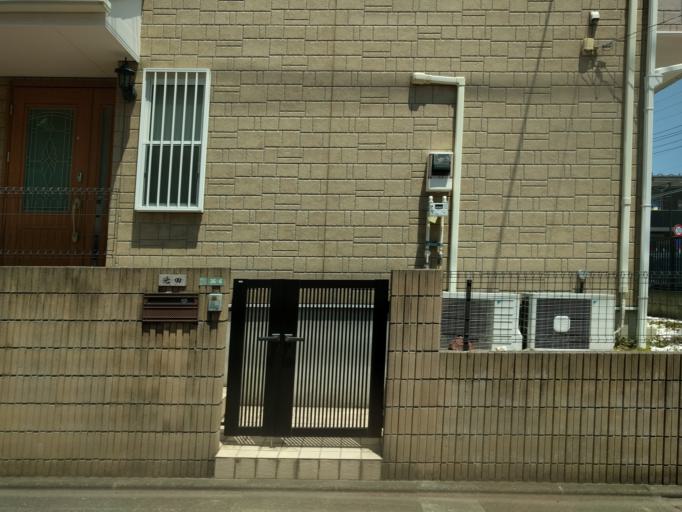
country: JP
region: Tokyo
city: Mitaka-shi
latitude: 35.6651
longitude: 139.6020
